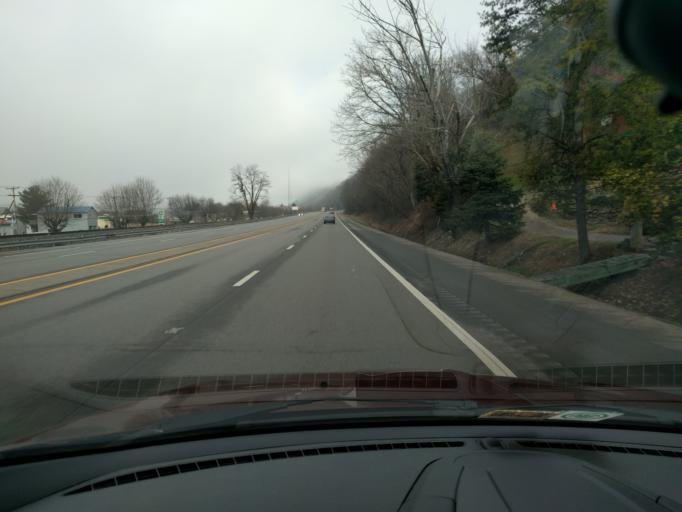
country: US
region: West Virginia
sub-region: Kanawha County
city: Belle
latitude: 38.2333
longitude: -81.5381
